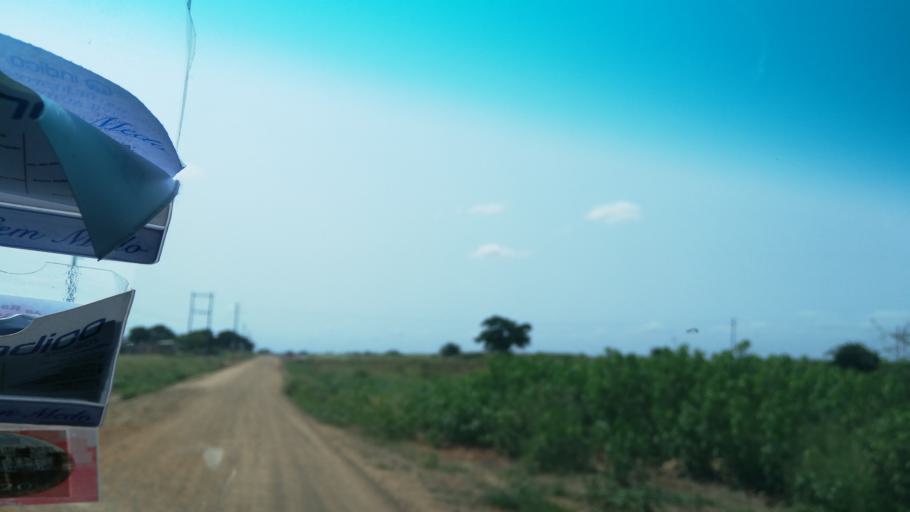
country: MZ
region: Maputo
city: Matola
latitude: -26.0672
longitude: 32.3904
